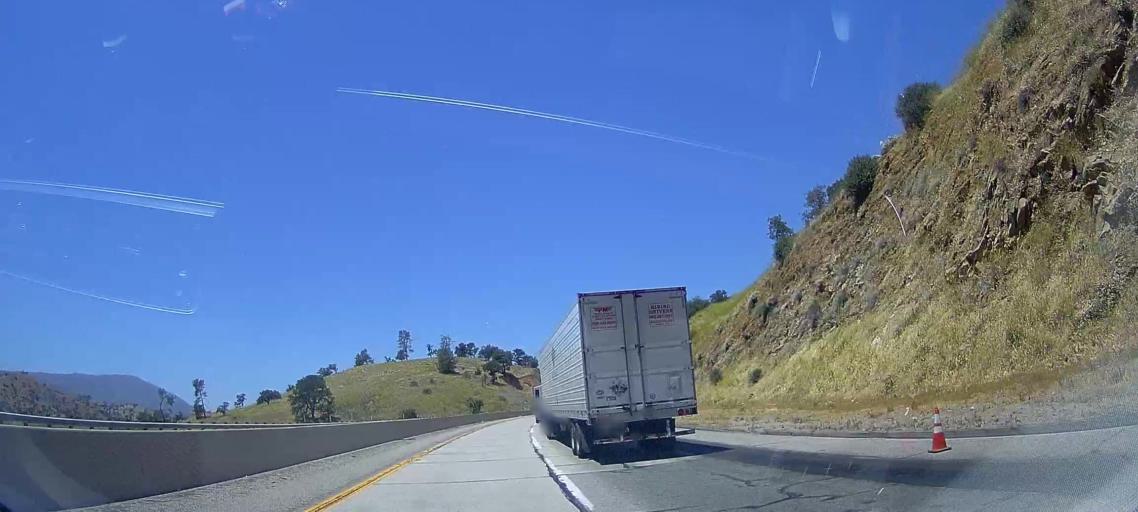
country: US
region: California
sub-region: Kern County
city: Golden Hills
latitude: 35.1861
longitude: -118.5030
